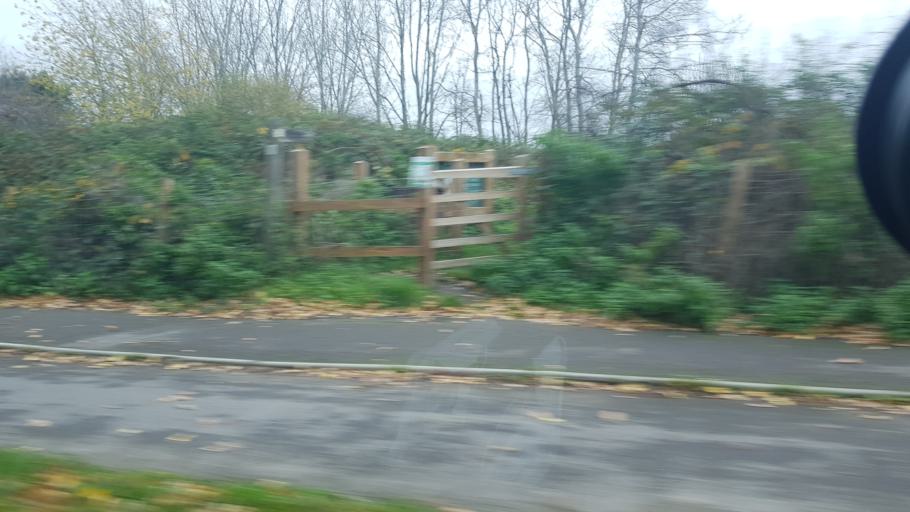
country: GB
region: England
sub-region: Hampshire
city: Farnborough
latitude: 51.2888
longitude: -0.7787
